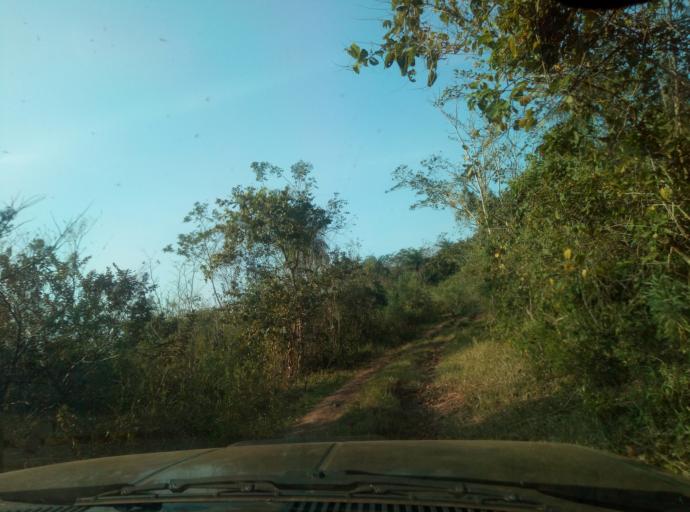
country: PY
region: Caaguazu
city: San Joaquin
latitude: -25.1567
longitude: -56.1220
